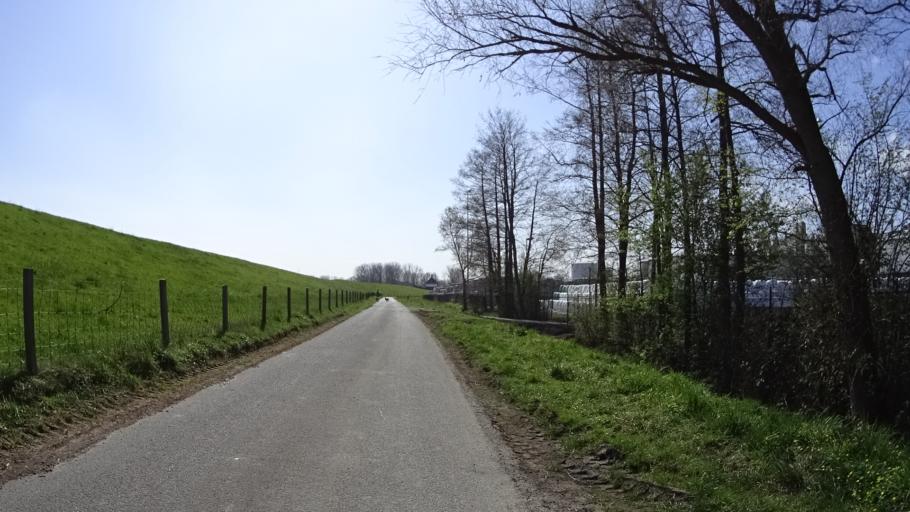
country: DE
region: Lower Saxony
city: Weener
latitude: 53.1706
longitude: 7.3685
